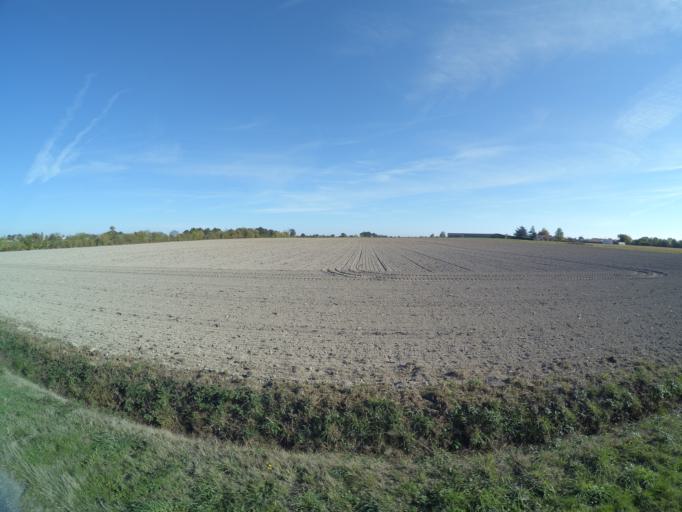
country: FR
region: Pays de la Loire
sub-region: Departement de la Loire-Atlantique
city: Saint-Lumine-de-Clisson
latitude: 47.0687
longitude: -1.3347
